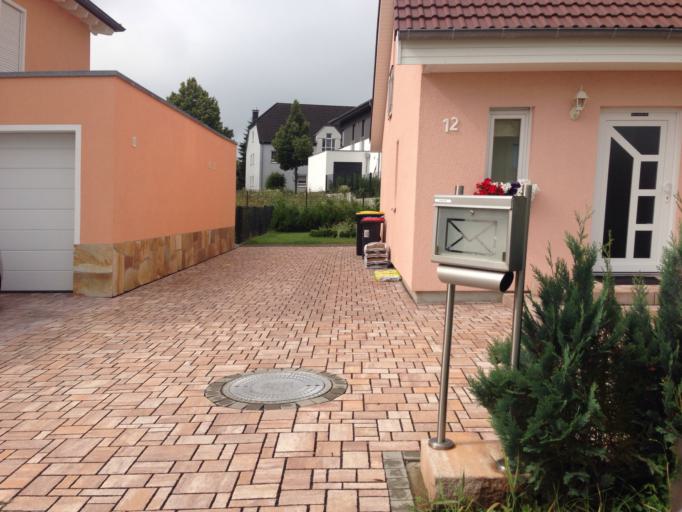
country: DE
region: Hesse
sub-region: Regierungsbezirk Darmstadt
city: Hanau am Main
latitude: 50.1009
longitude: 8.9181
